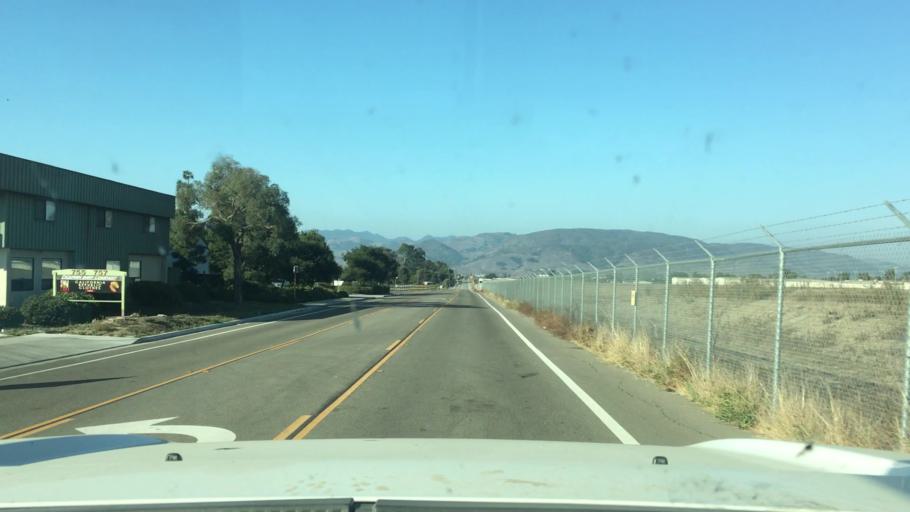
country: US
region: California
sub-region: San Luis Obispo County
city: San Luis Obispo
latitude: 35.2359
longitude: -120.6419
